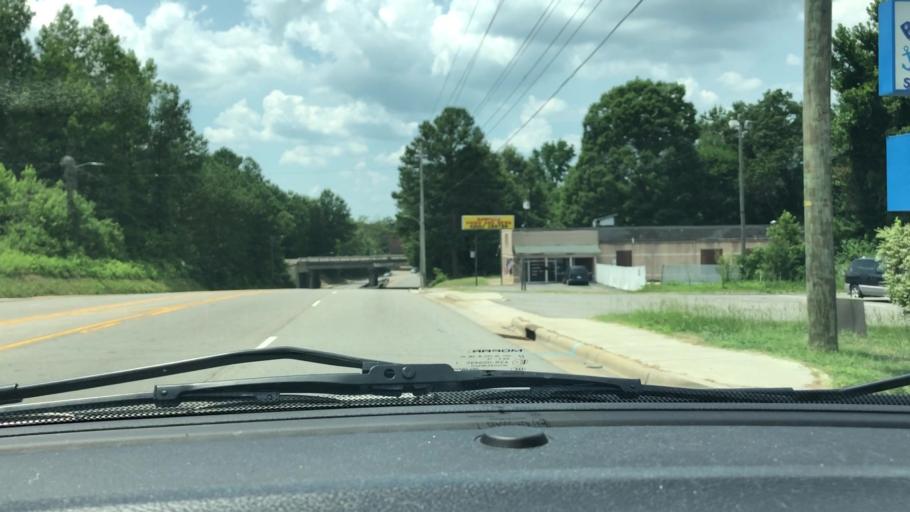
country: US
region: North Carolina
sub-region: Lee County
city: Sanford
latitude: 35.4721
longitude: -79.1747
